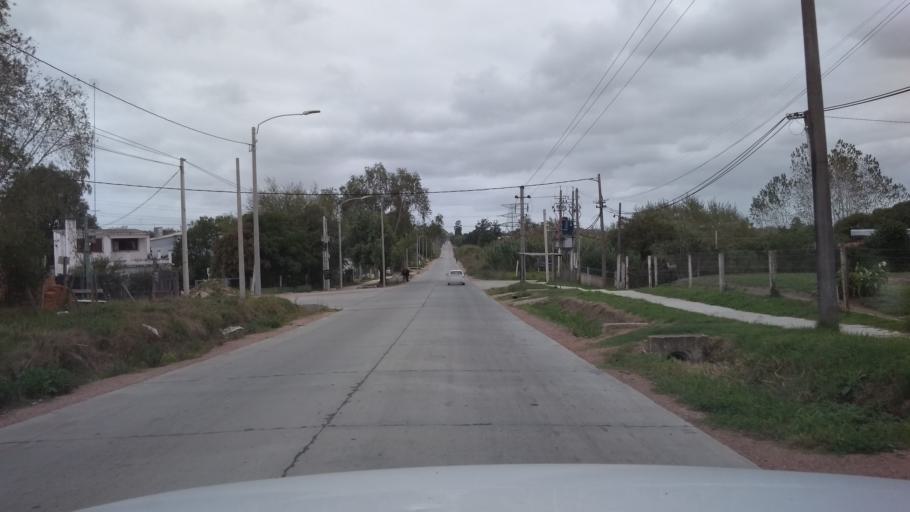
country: UY
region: Canelones
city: Toledo
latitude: -34.7895
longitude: -56.1449
